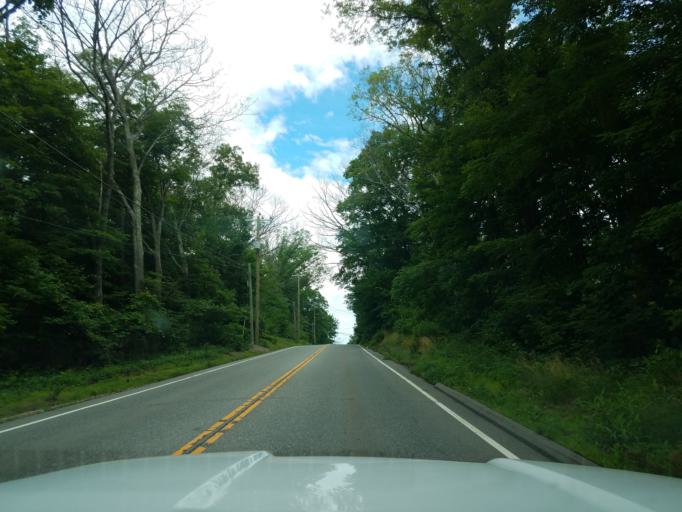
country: US
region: Connecticut
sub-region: Tolland County
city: Mansfield City
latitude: 41.7727
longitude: -72.2053
